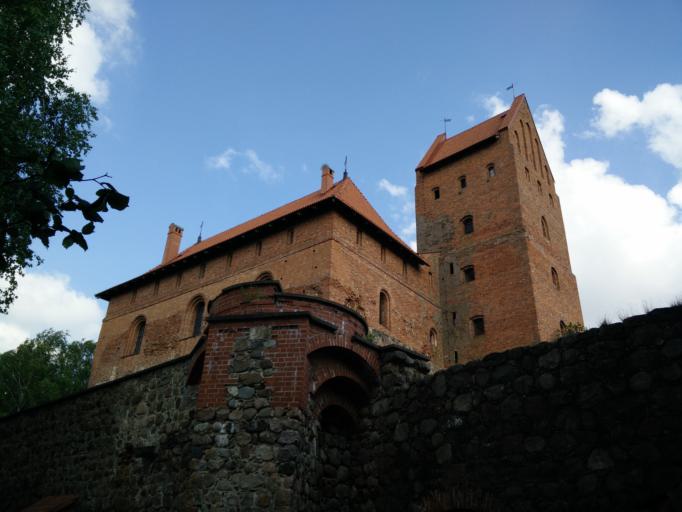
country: LT
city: Trakai
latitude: 54.6529
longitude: 24.9334
